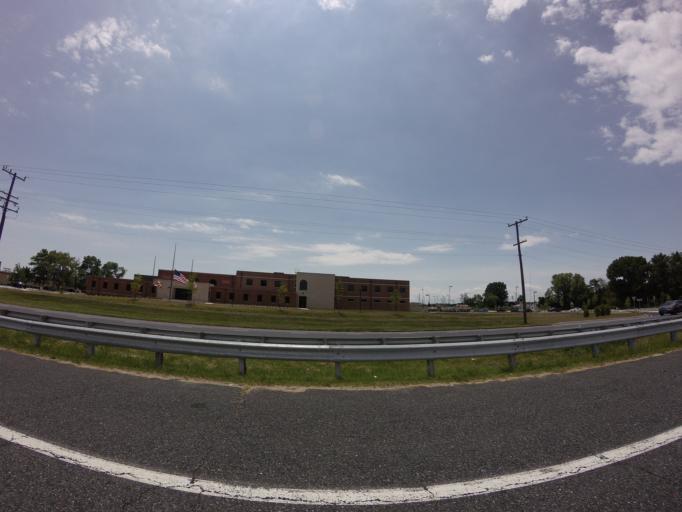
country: US
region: Maryland
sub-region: Baltimore County
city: Essex
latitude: 39.2873
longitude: -76.4988
